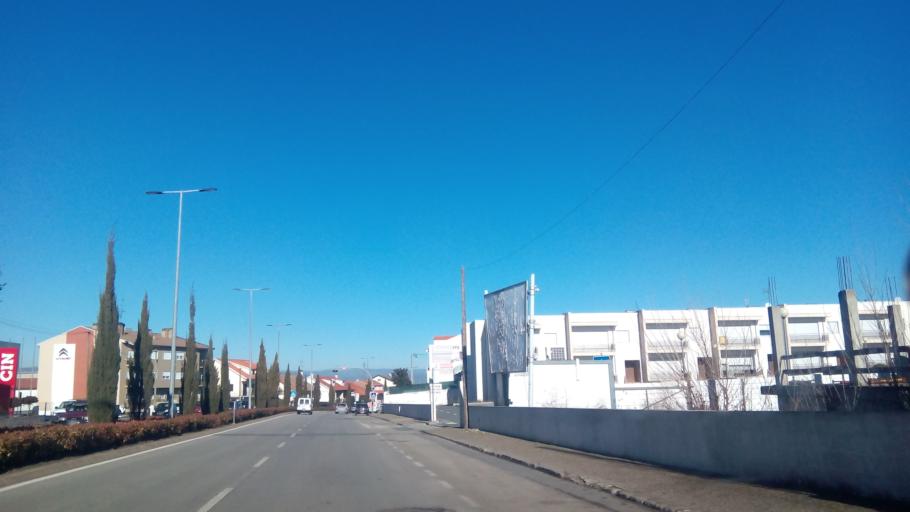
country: PT
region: Braganca
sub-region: Braganca Municipality
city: Braganca
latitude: 41.7811
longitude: -6.7786
